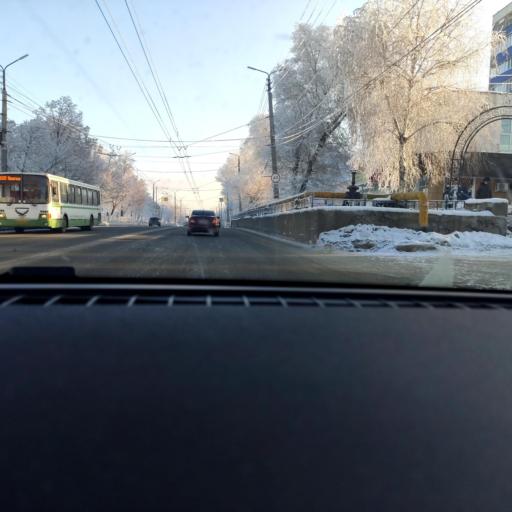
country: RU
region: Samara
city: Novokuybyshevsk
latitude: 53.1004
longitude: 49.9595
